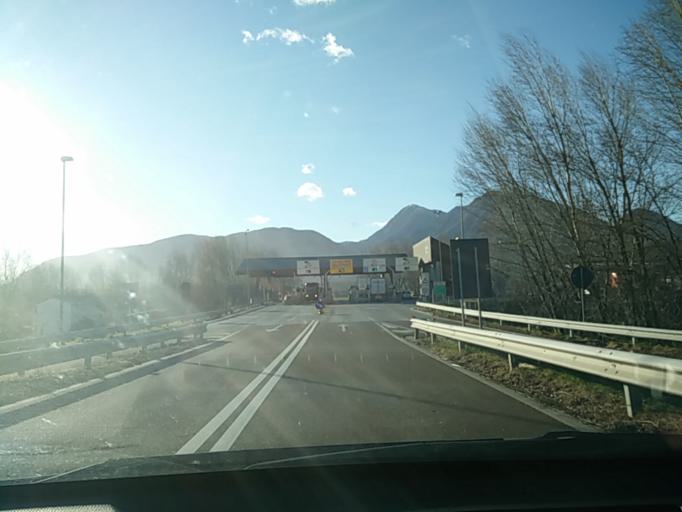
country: IT
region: Friuli Venezia Giulia
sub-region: Provincia di Udine
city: Osoppo
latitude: 46.2501
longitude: 13.0995
